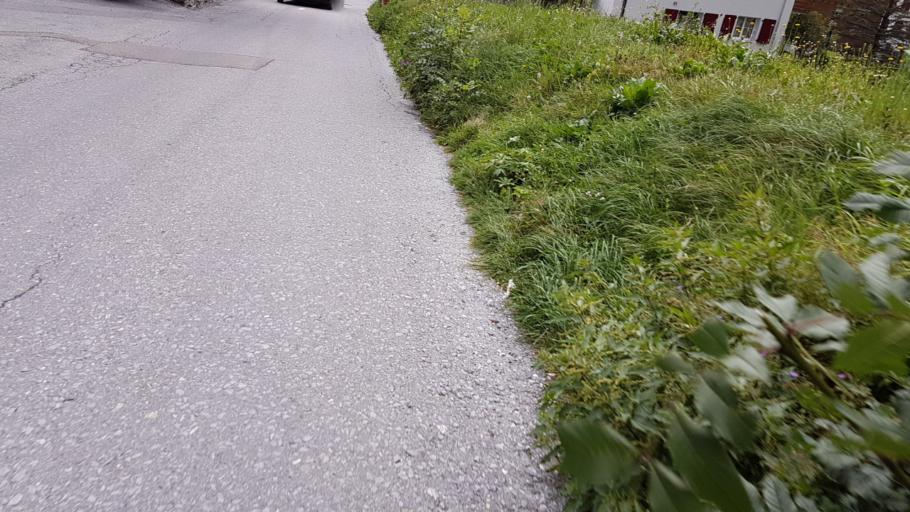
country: CH
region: Valais
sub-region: Leuk District
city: Leukerbad
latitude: 46.3834
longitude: 7.6247
